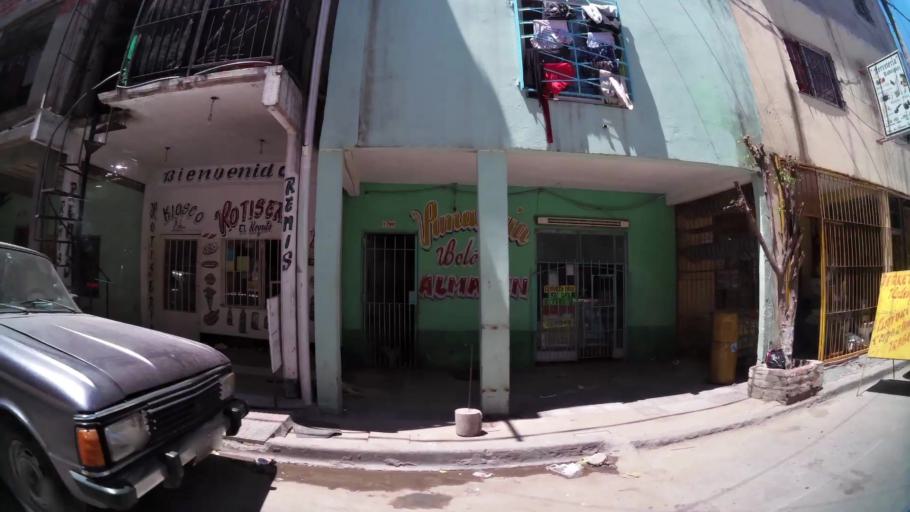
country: AR
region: Buenos Aires
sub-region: Partido de Avellaneda
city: Avellaneda
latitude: -34.6546
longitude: -58.4000
